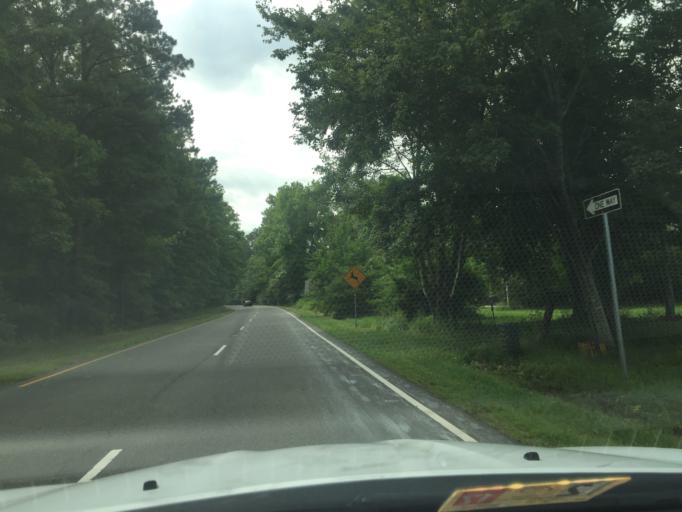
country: US
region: Virginia
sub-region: Charles City County
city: Charles City
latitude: 37.4516
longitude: -77.0780
